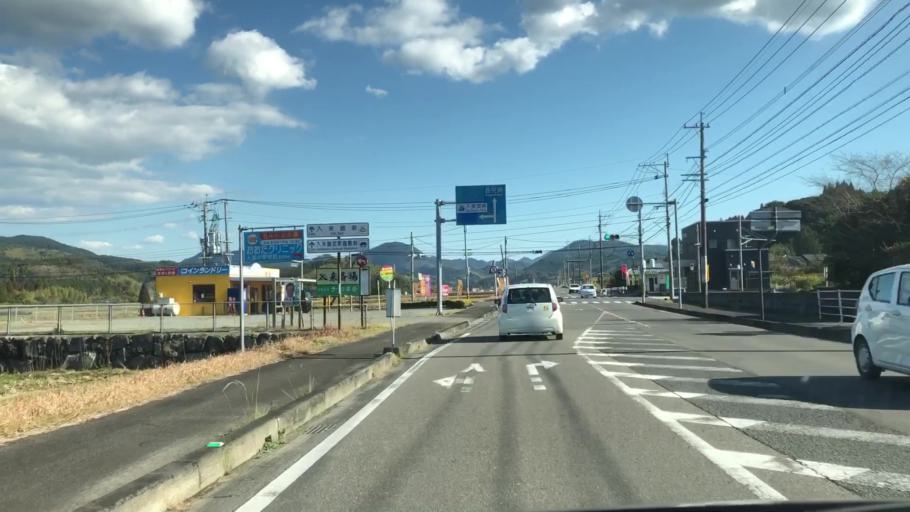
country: JP
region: Kagoshima
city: Satsumasendai
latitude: 31.7986
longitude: 130.4316
